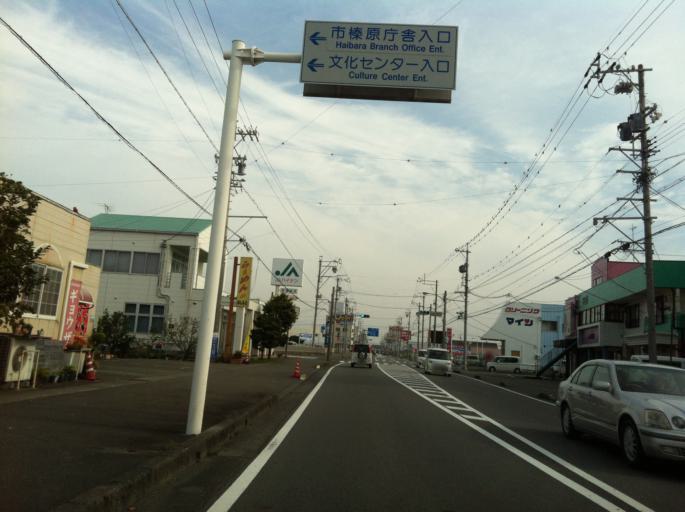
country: JP
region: Shizuoka
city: Sagara
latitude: 34.7365
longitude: 138.2294
